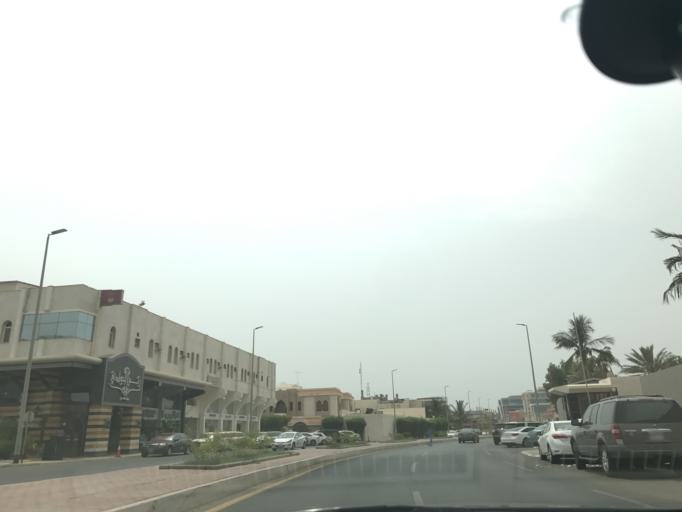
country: SA
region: Makkah
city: Jeddah
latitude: 21.5582
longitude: 39.1483
